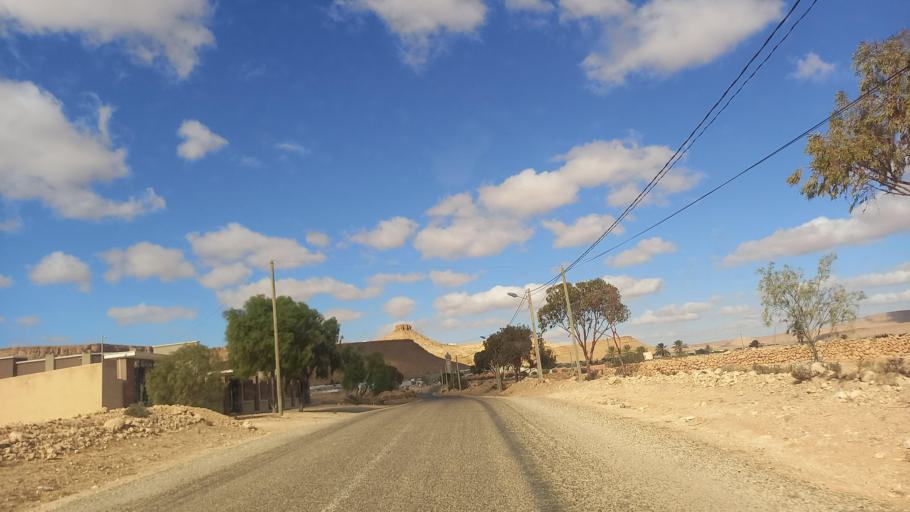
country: TN
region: Tataouine
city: Tataouine
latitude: 32.9790
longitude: 10.2731
